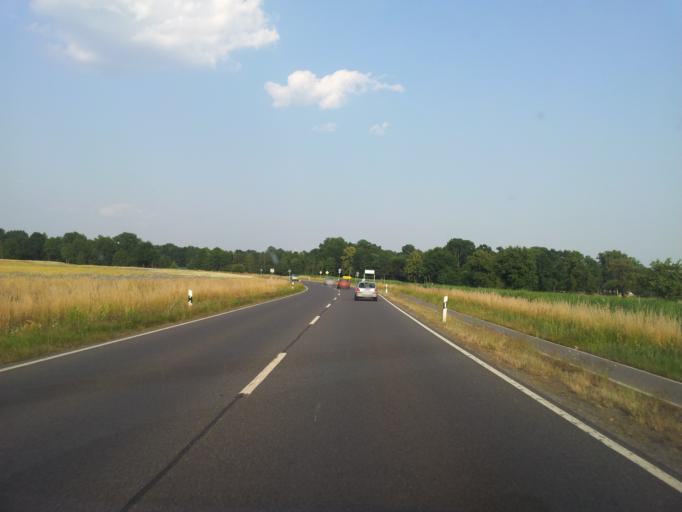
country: DE
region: Saxony
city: Hoyerswerda
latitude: 51.4241
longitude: 14.2313
